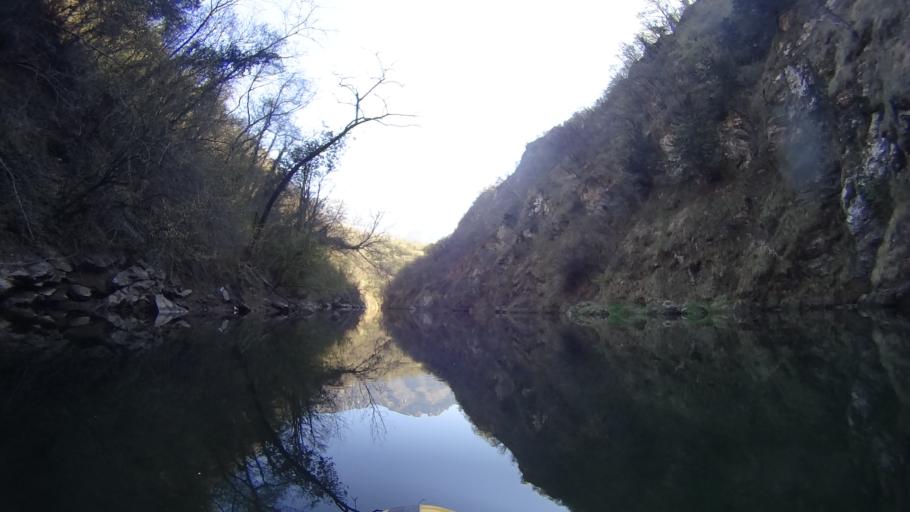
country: IT
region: Veneto
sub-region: Provincia di Vicenza
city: Cogollo del Cengio
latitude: 45.7767
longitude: 11.4095
